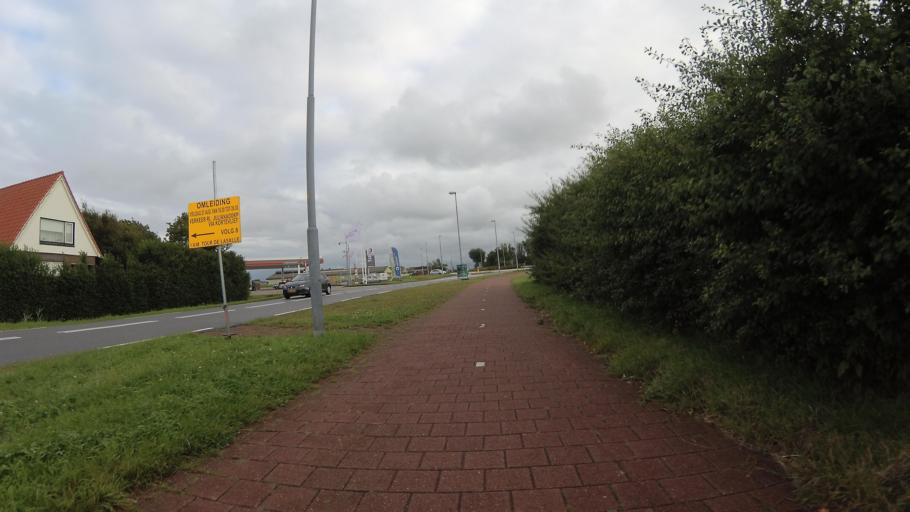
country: NL
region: North Holland
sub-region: Gemeente Den Helder
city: Den Helder
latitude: 52.9302
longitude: 4.7558
